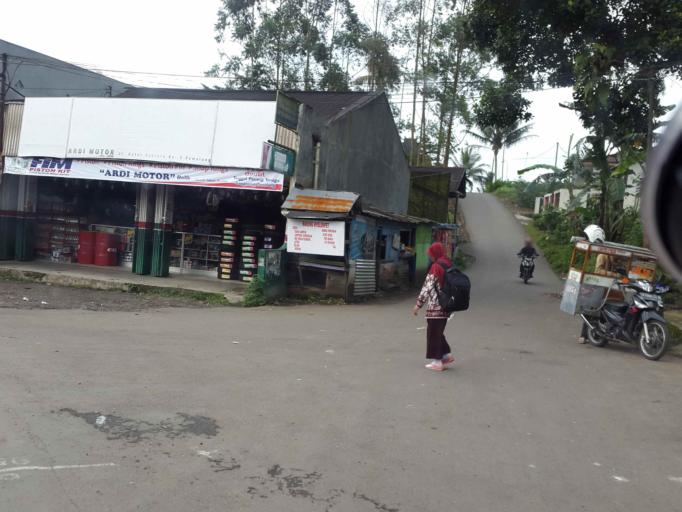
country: ID
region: Central Java
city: Randudongkal
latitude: -7.1879
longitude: 109.3300
